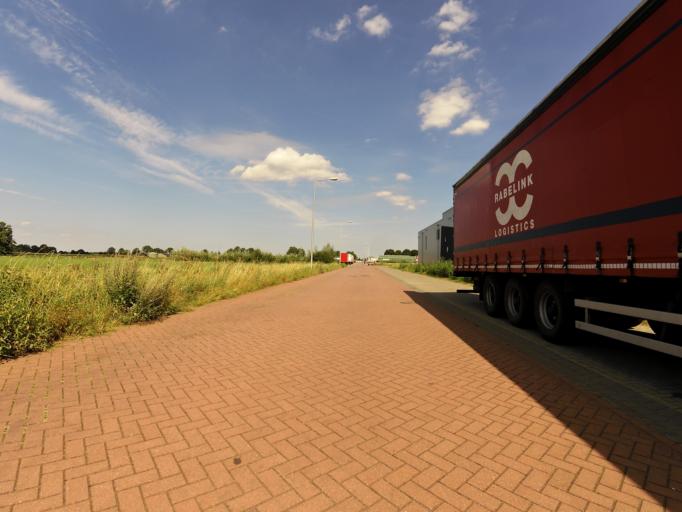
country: NL
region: Gelderland
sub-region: Gemeente Montferland
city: s-Heerenberg
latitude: 51.9209
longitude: 6.1842
